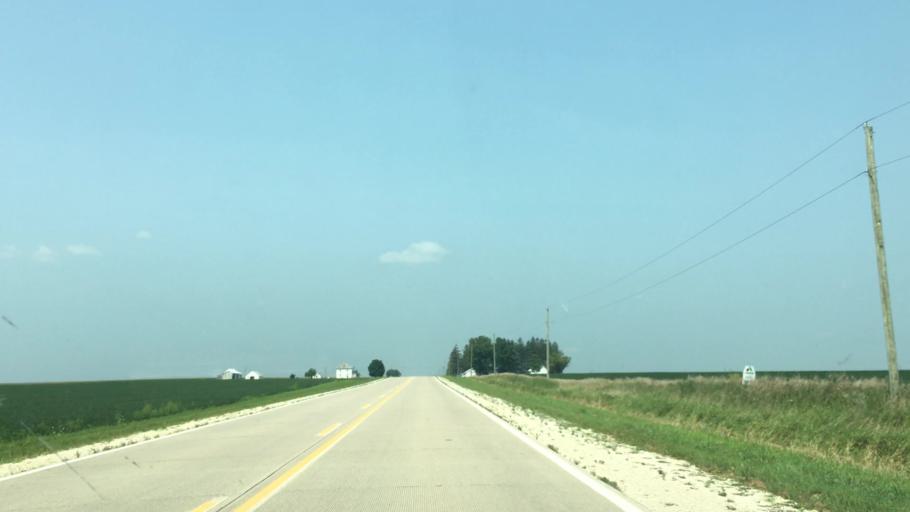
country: US
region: Iowa
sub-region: Fayette County
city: Oelwein
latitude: 42.7067
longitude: -91.8048
